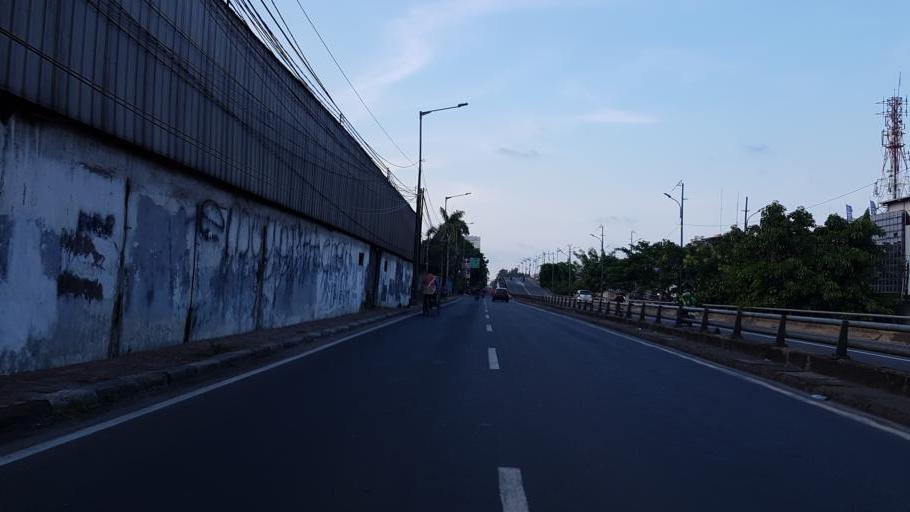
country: ID
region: Jakarta Raya
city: Jakarta
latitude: -6.1399
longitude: 106.7931
